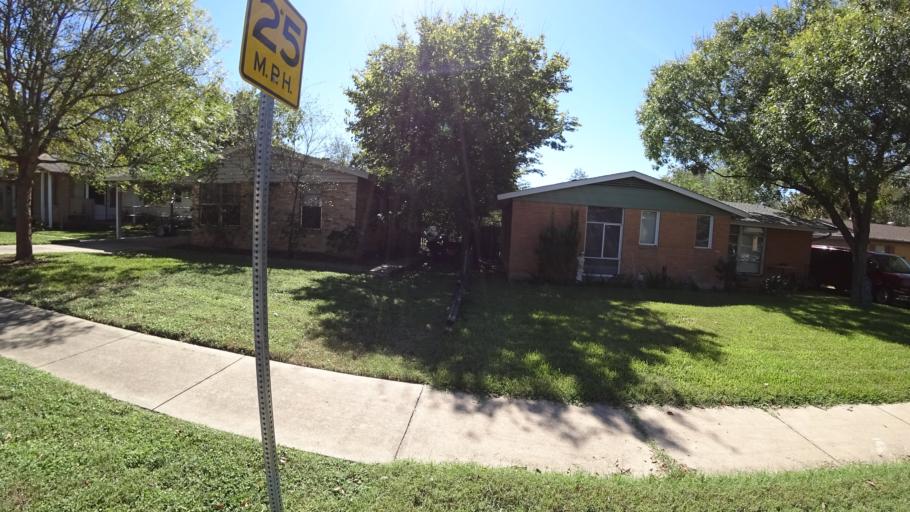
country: US
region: Texas
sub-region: Travis County
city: Rollingwood
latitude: 30.2248
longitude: -97.7889
